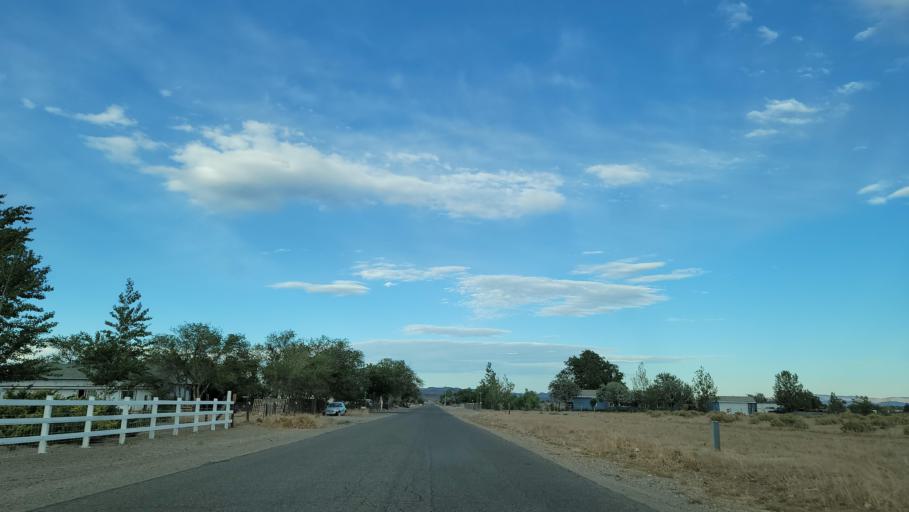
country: US
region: Nevada
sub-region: Lyon County
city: Silver Springs
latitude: 39.3899
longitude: -119.2418
